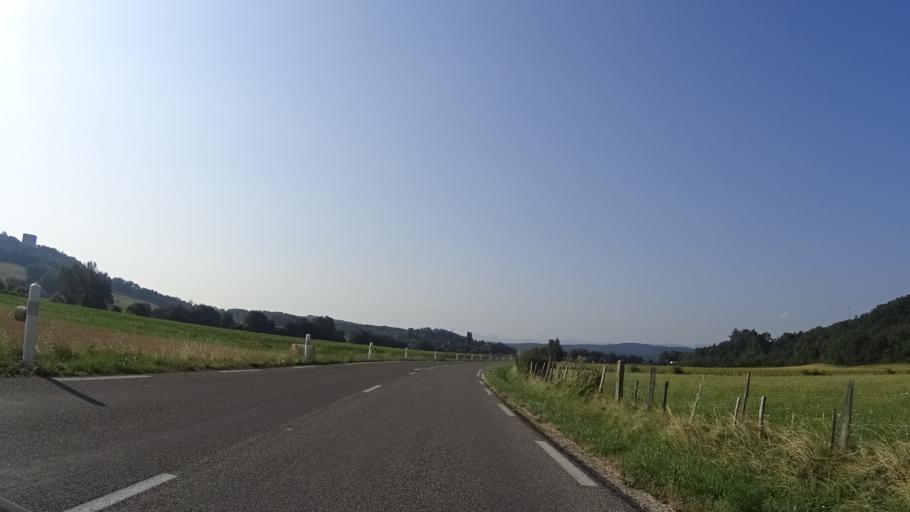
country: FR
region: Midi-Pyrenees
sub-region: Departement de l'Ariege
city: Mirepoix
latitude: 43.0415
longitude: 1.8969
